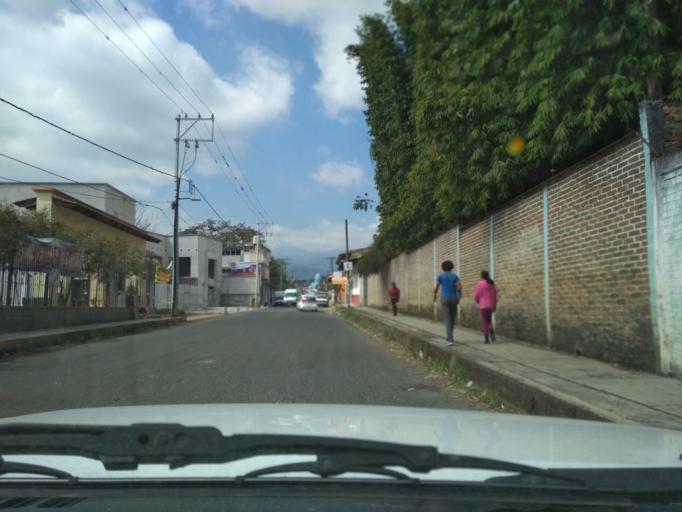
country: MX
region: Veracruz
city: Coatepec
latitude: 19.4509
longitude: -96.9473
